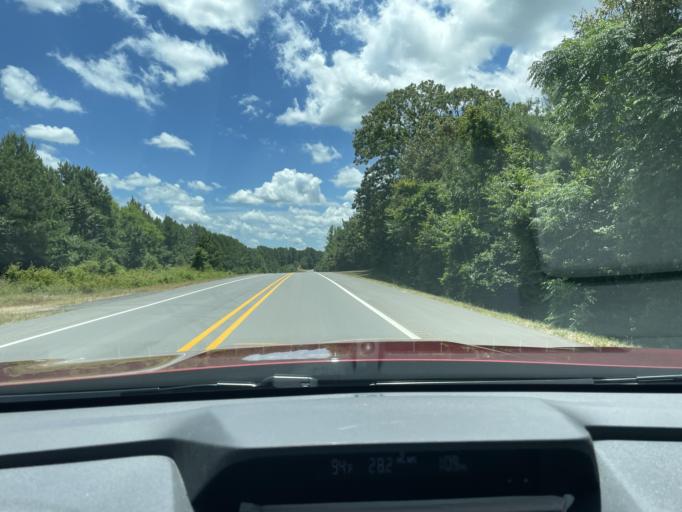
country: US
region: Arkansas
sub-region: Drew County
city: Monticello
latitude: 33.7266
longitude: -91.8121
